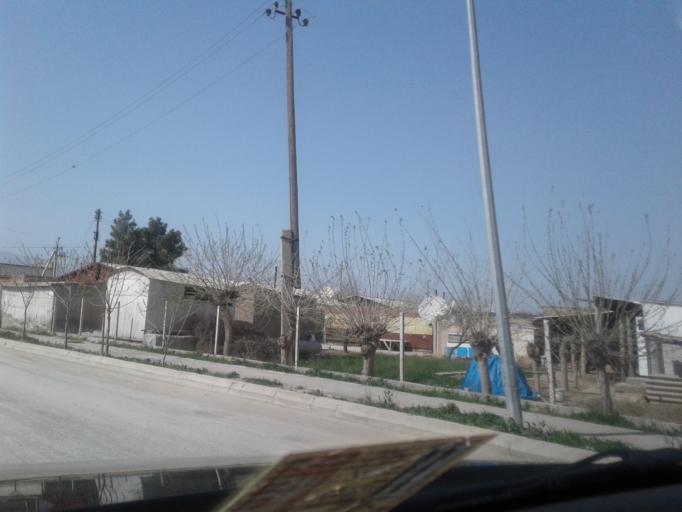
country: TM
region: Ahal
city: Abadan
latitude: 38.1640
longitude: 57.9867
